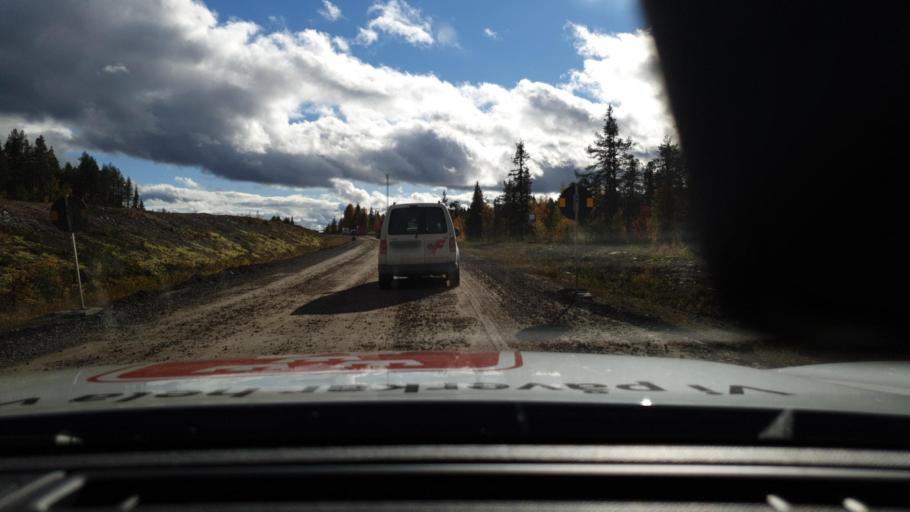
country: SE
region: Norrbotten
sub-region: Gallivare Kommun
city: Malmberget
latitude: 67.1985
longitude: 20.9809
